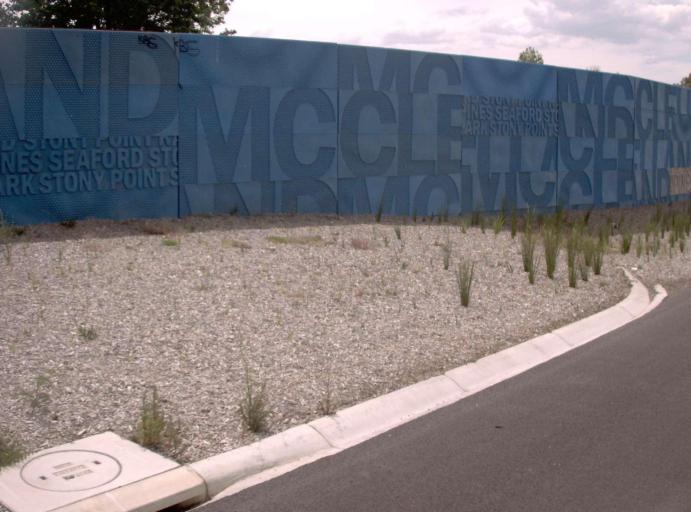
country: AU
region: Victoria
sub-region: Frankston
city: Langwarrin
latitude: -38.1453
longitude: 145.1727
